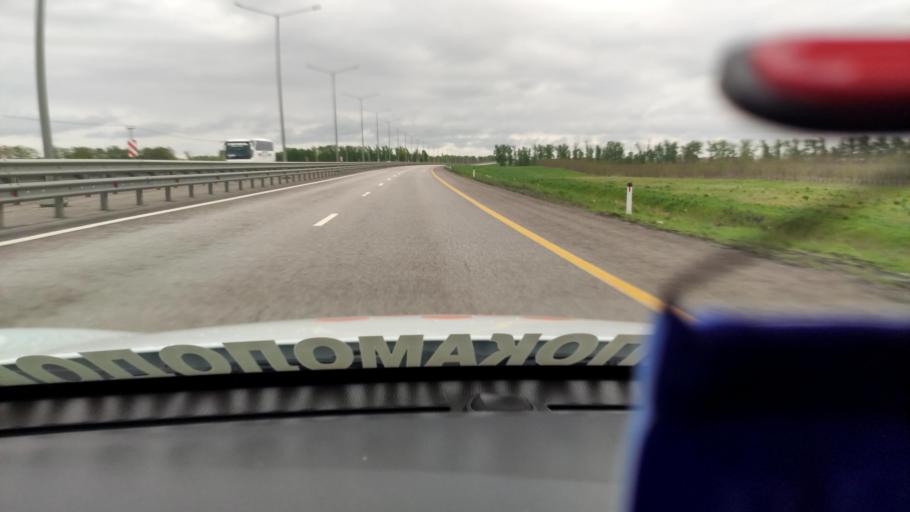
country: RU
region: Voronezj
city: Podkletnoye
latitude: 51.5829
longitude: 39.4568
